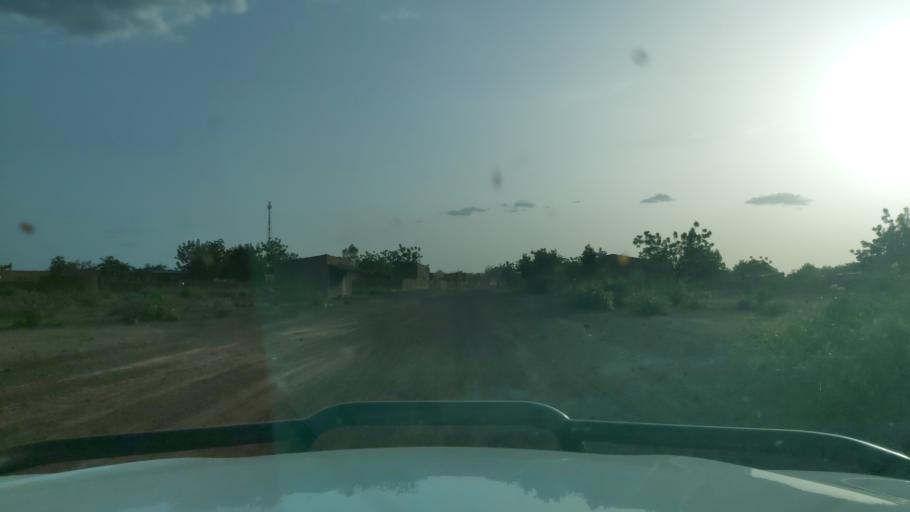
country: ML
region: Koulikoro
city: Kolokani
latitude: 13.2038
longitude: -7.9267
